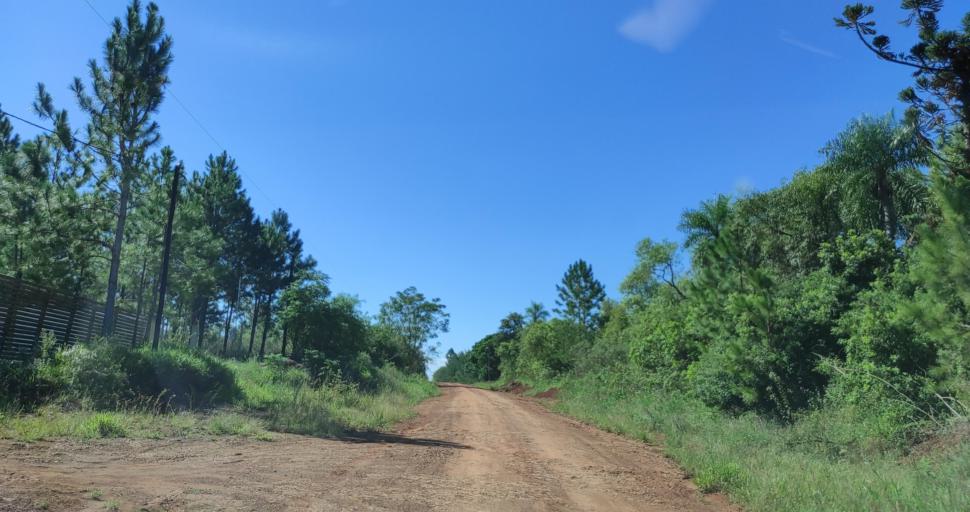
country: AR
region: Misiones
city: Garupa
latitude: -27.4745
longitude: -55.7987
